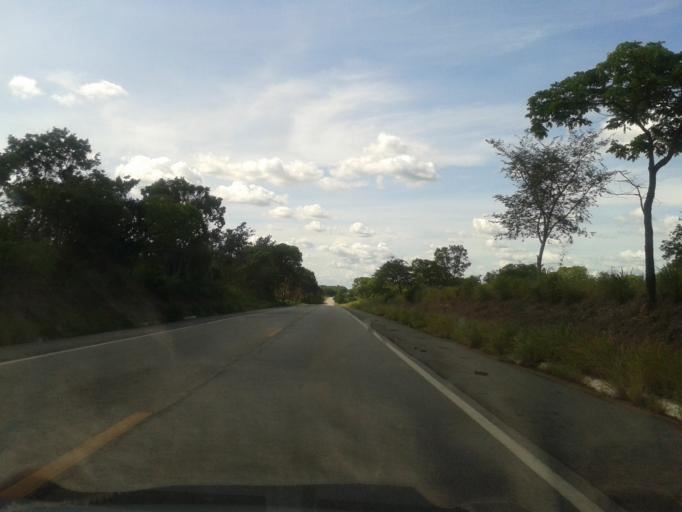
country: BR
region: Goias
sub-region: Mozarlandia
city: Mozarlandia
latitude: -15.2238
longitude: -50.5256
